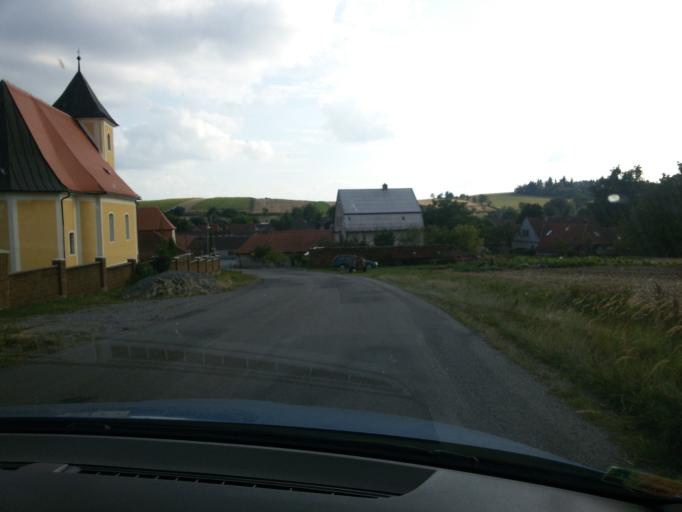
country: CZ
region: South Moravian
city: Olesnice
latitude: 49.4856
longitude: 16.4246
